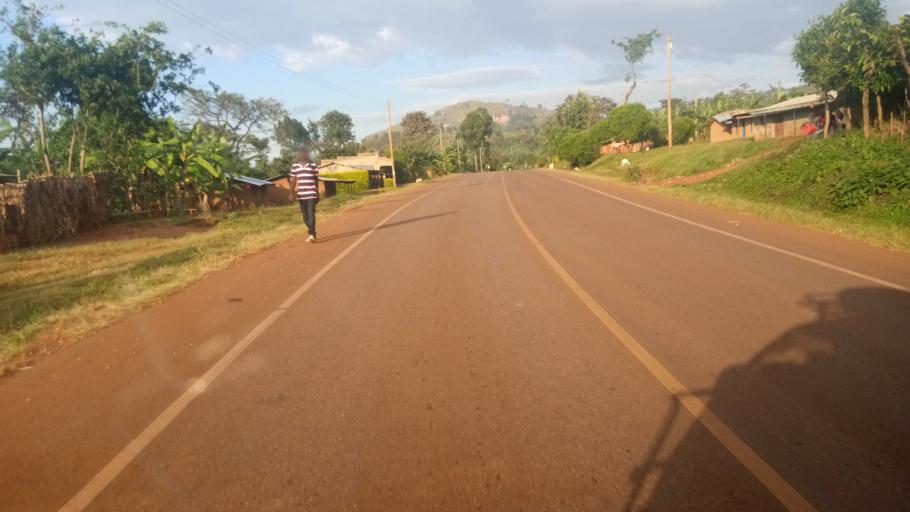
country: UG
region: Eastern Region
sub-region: Sironko District
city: Sironko
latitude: 1.3214
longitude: 34.3437
